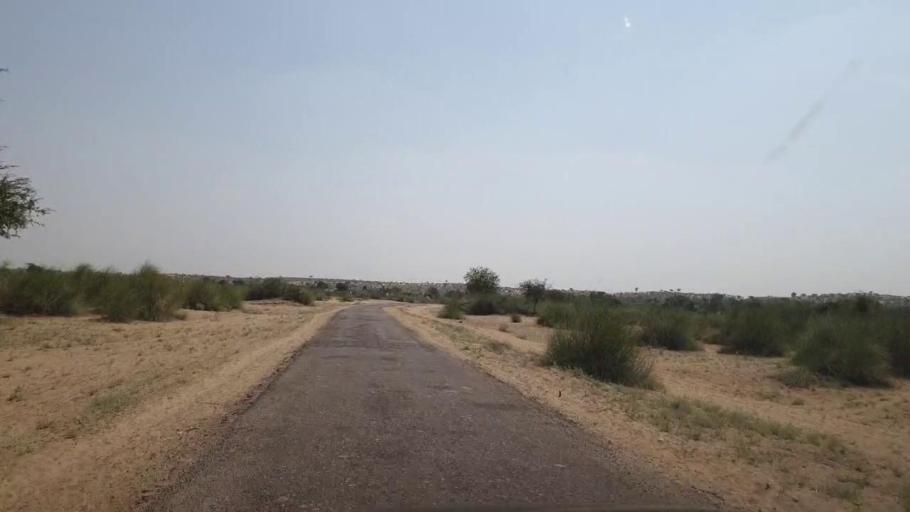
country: PK
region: Sindh
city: Islamkot
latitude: 25.0725
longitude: 70.7428
